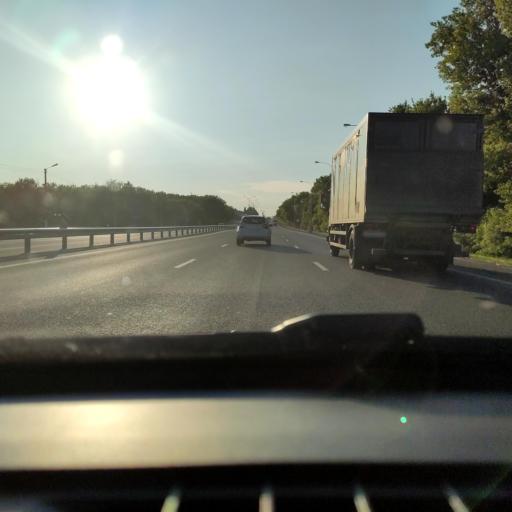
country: RU
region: Voronezj
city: Novaya Usman'
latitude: 51.6232
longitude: 39.3589
